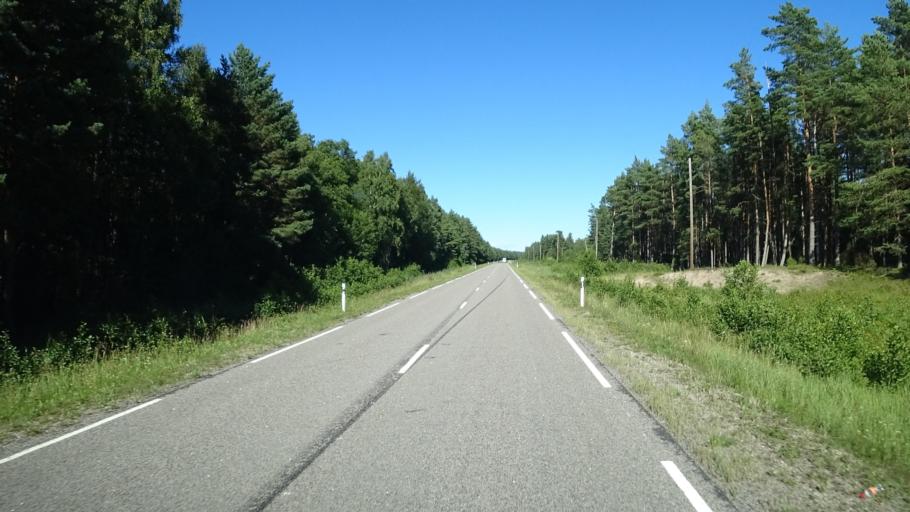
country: LV
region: Dundaga
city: Dundaga
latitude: 57.7121
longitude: 22.4518
